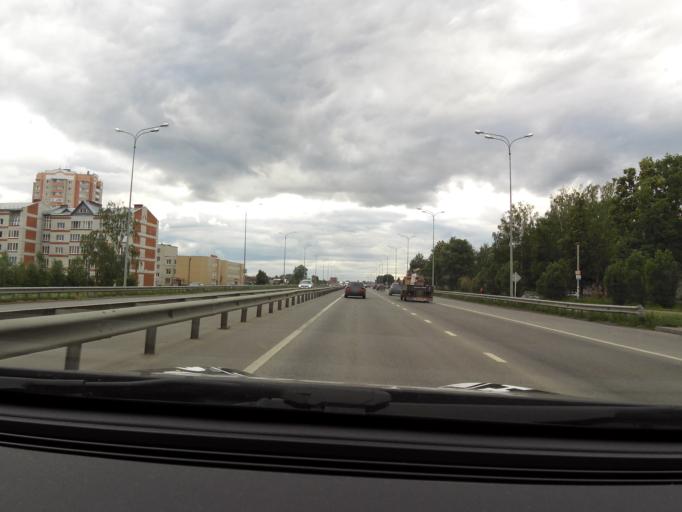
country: RU
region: Tatarstan
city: Osinovo
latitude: 55.8483
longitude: 48.9063
